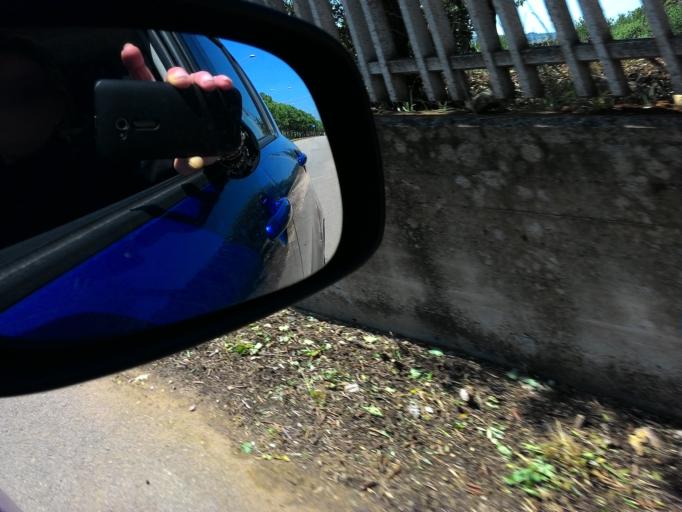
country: IT
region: Apulia
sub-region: Provincia di Bari
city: Putignano
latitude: 40.8487
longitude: 17.1405
